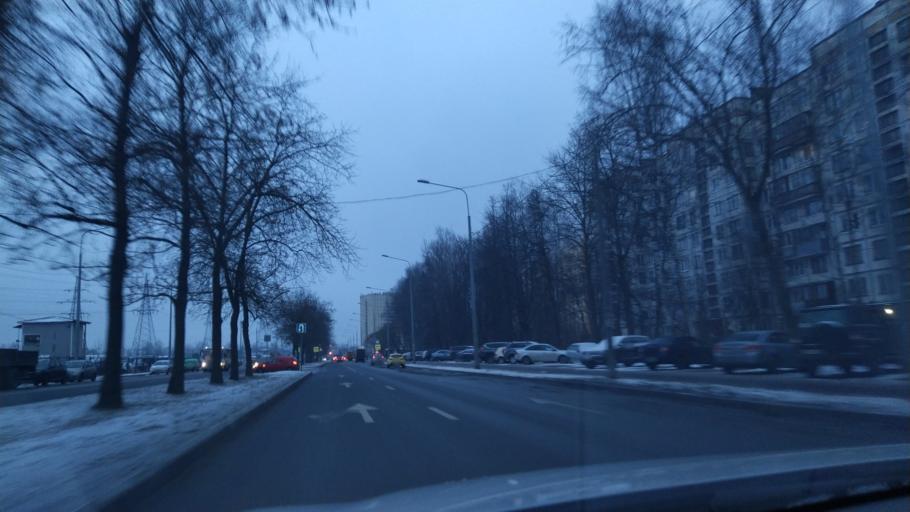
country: RU
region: St.-Petersburg
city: Grazhdanka
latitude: 60.0168
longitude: 30.4260
